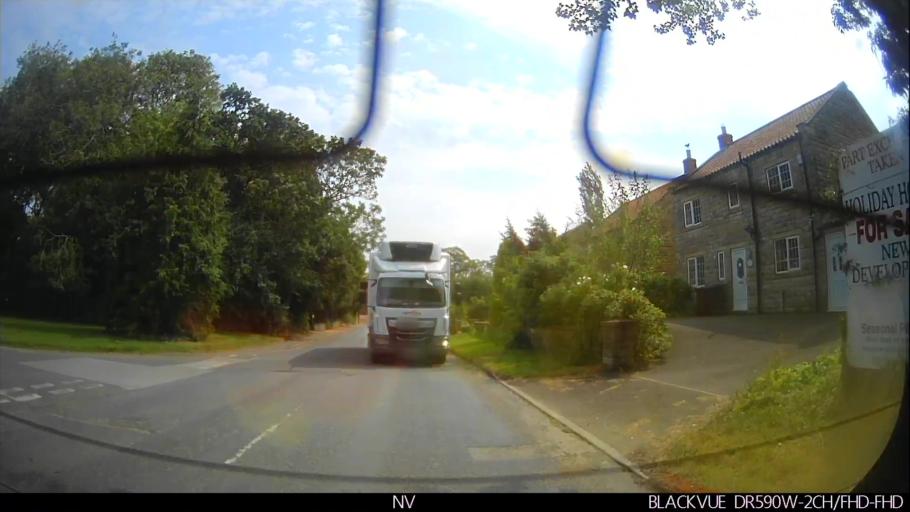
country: GB
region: England
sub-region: North Yorkshire
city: Great Habton
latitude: 54.2054
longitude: -0.8090
